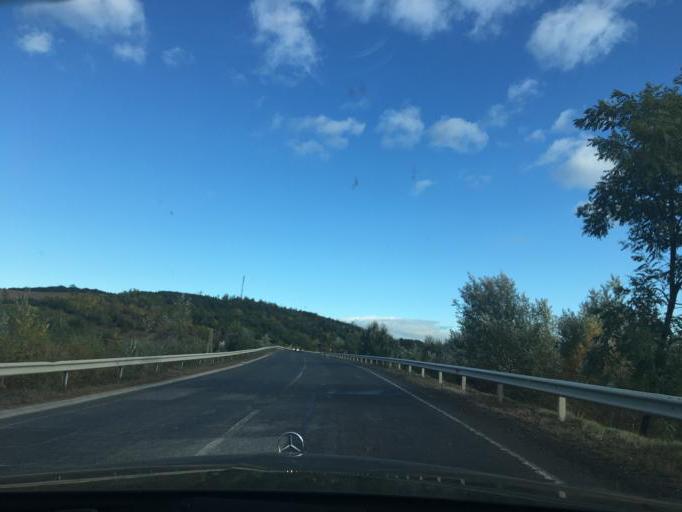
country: HU
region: Borsod-Abauj-Zemplen
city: Gonc
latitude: 48.4841
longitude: 21.2112
